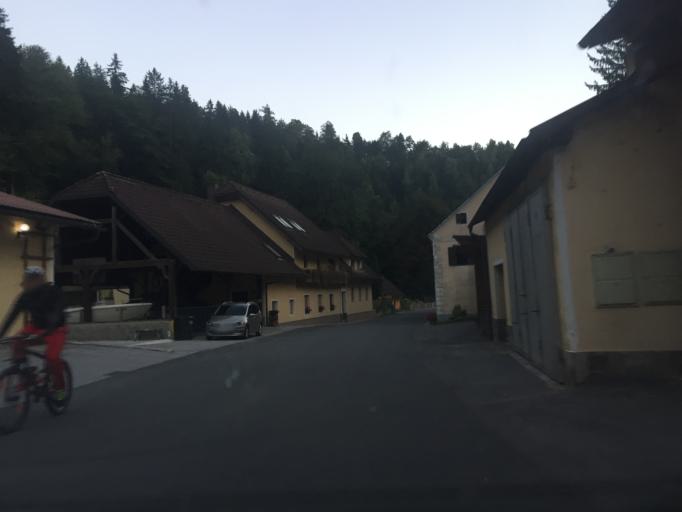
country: SI
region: Sostanj
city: Topolsica
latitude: 46.3777
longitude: 15.0251
